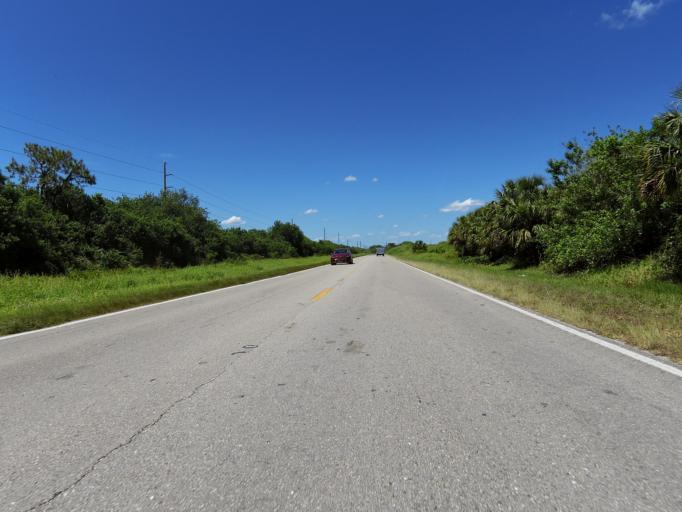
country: US
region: Florida
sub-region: Collier County
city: Immokalee
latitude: 26.3607
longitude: -81.4167
